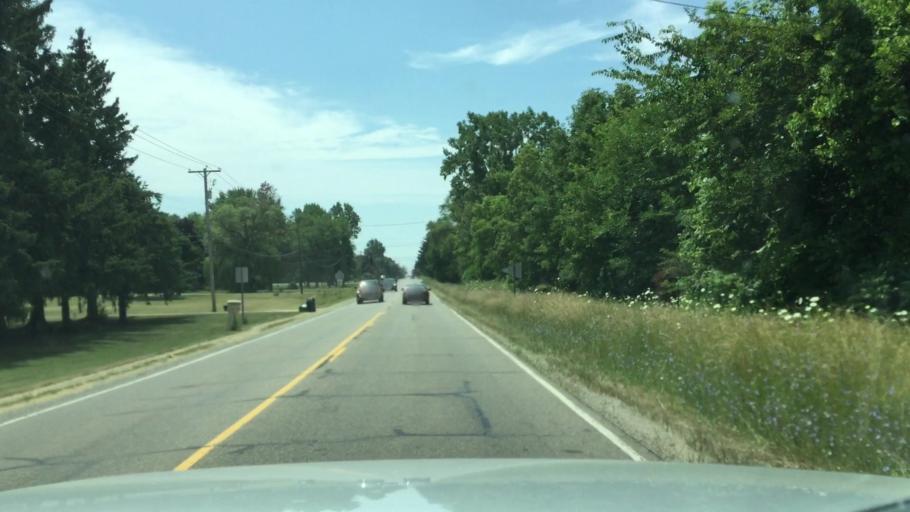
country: US
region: Michigan
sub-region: Genesee County
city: Swartz Creek
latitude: 43.0145
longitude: -83.7830
